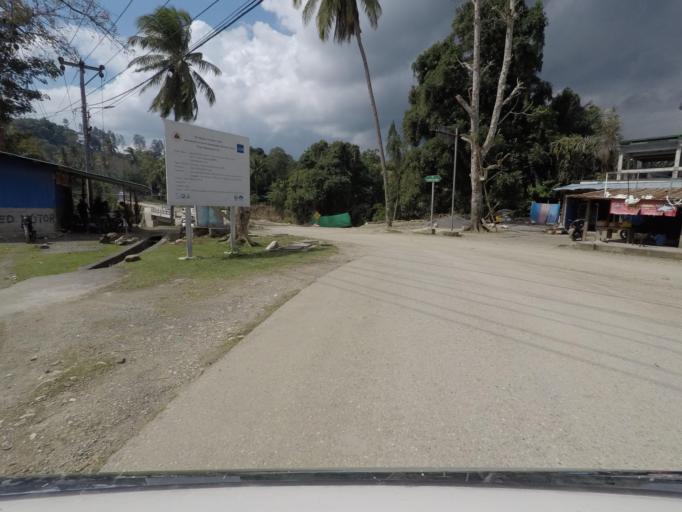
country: TL
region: Viqueque
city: Viqueque
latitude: -8.8494
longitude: 126.3661
